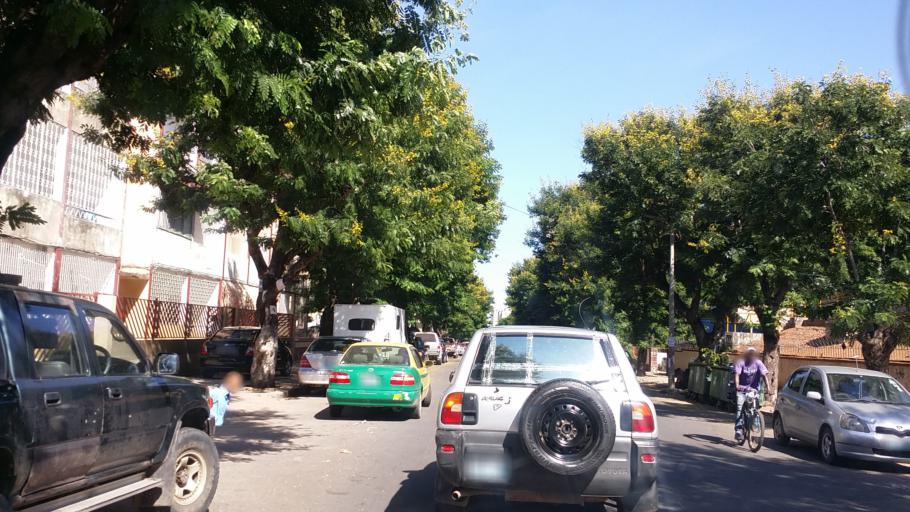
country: MZ
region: Maputo City
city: Maputo
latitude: -25.9698
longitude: 32.5835
